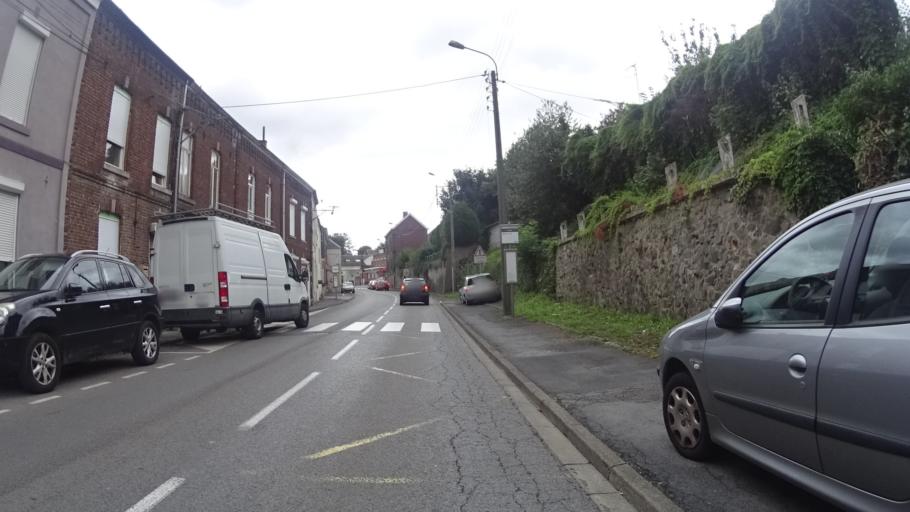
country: FR
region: Nord-Pas-de-Calais
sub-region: Departement du Nord
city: Hautmont
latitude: 50.2485
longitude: 3.9152
